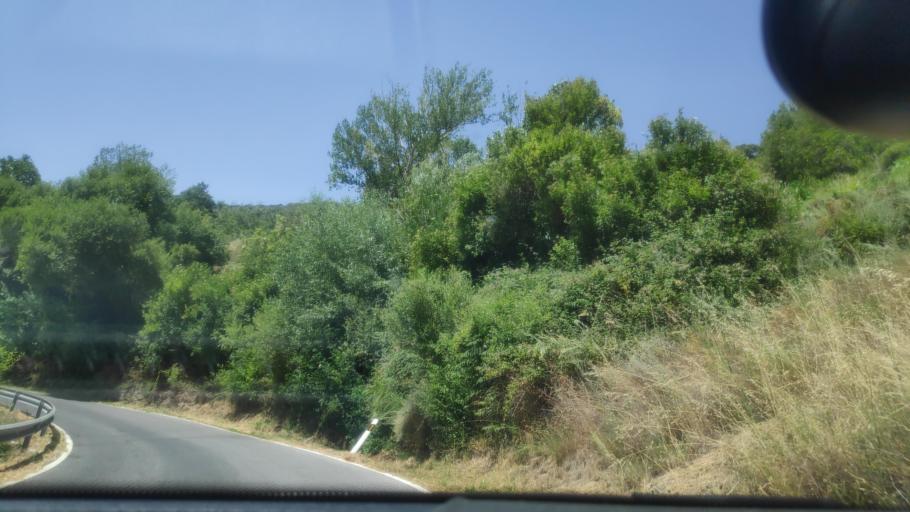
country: ES
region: Andalusia
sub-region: Provincia de Granada
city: Trevelez
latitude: 36.9980
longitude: -3.2673
